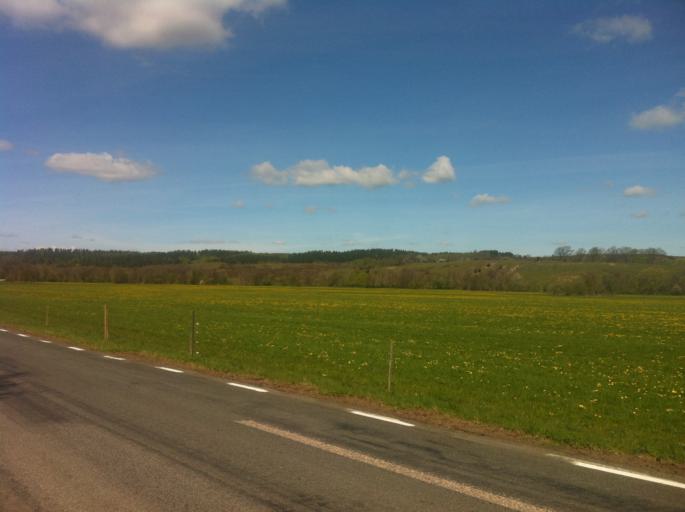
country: SE
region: Skane
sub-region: Kristianstads Kommun
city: Degeberga
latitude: 55.7274
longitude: 14.0922
